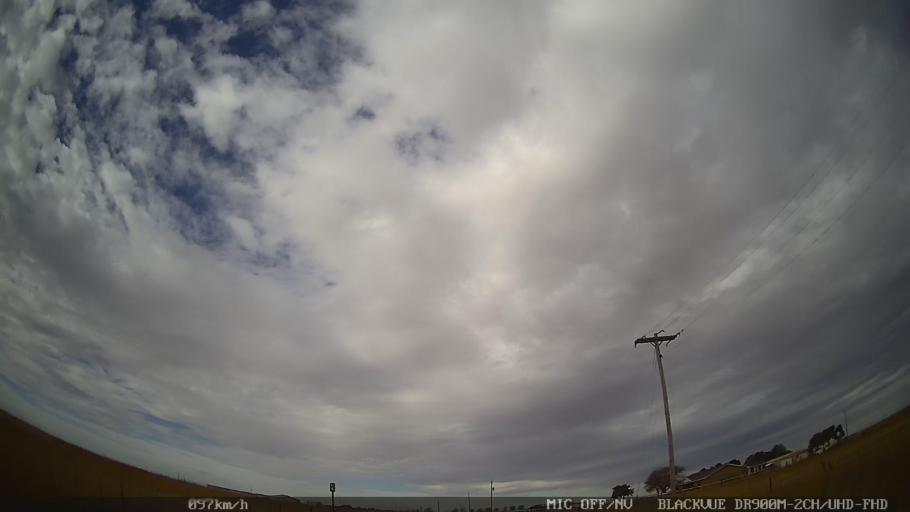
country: US
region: New Mexico
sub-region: Curry County
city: Clovis
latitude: 34.4192
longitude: -103.1277
